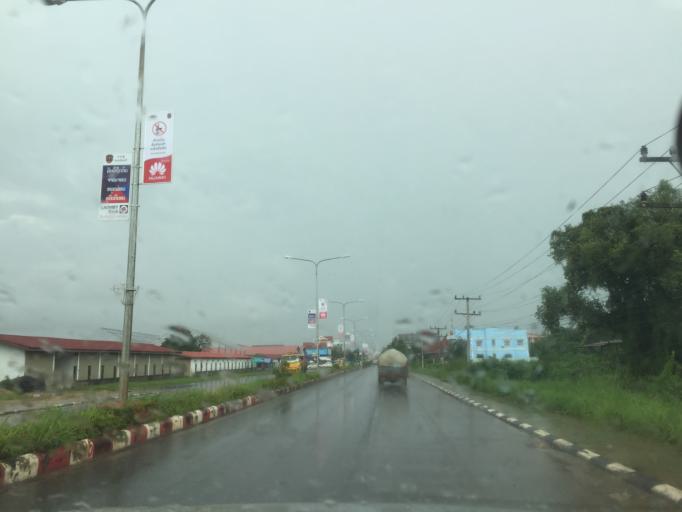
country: LA
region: Attapu
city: Attapu
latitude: 14.8178
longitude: 106.8170
